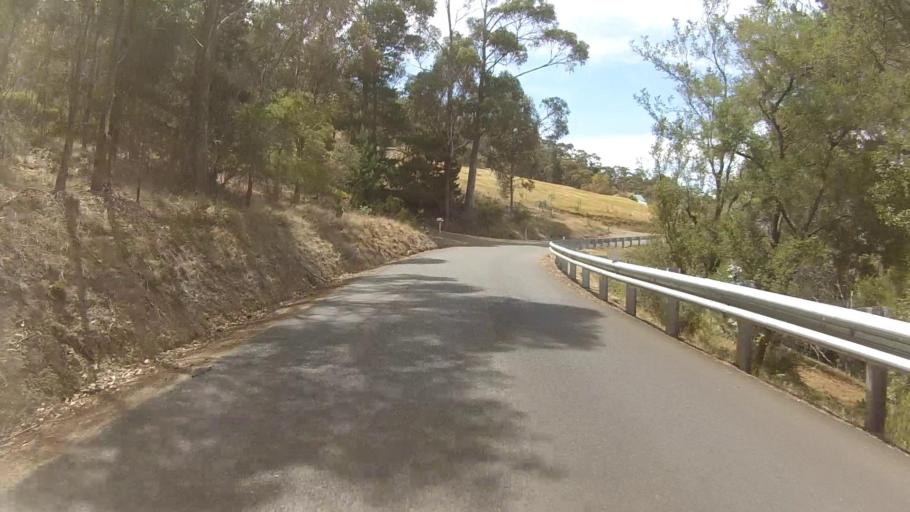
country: AU
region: Tasmania
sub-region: Kingborough
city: Blackmans Bay
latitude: -43.0556
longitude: 147.3349
